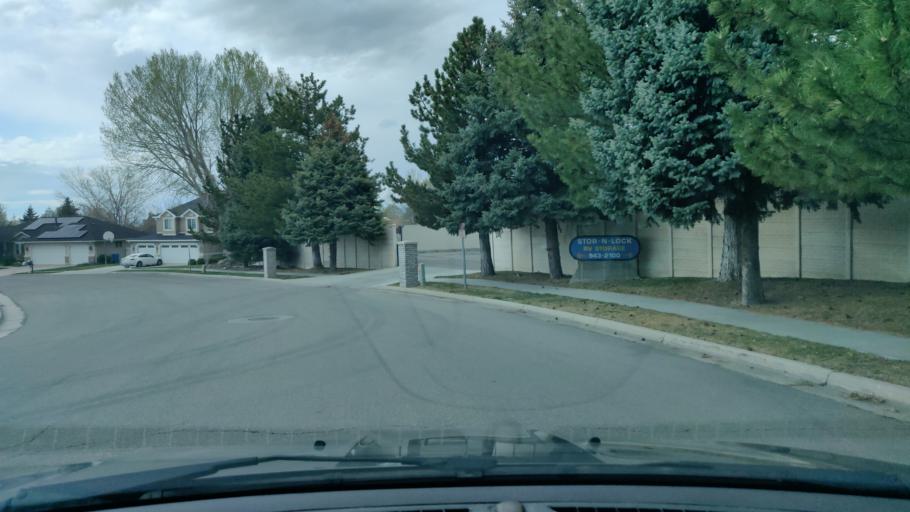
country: US
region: Utah
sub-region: Salt Lake County
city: Cottonwood Heights
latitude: 40.6263
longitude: -111.8272
